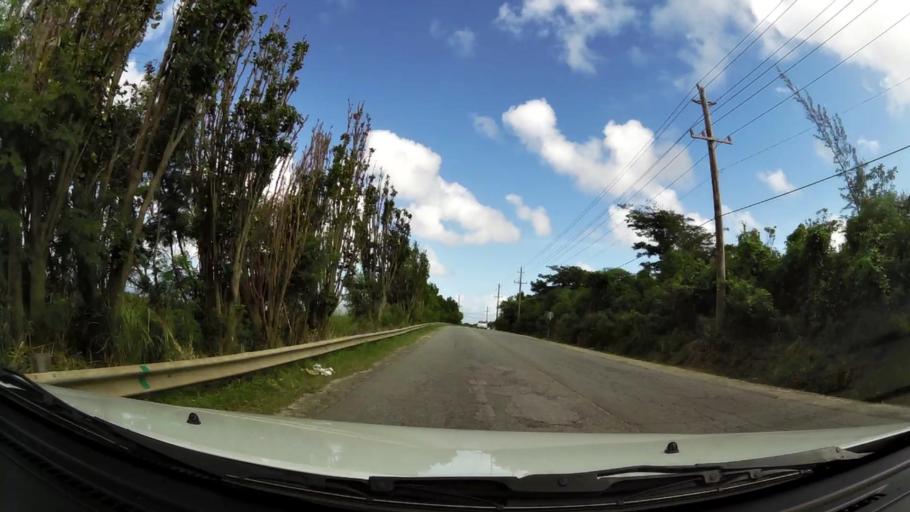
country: BB
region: Saint Peter
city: Speightstown
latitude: 13.2453
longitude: -59.6249
